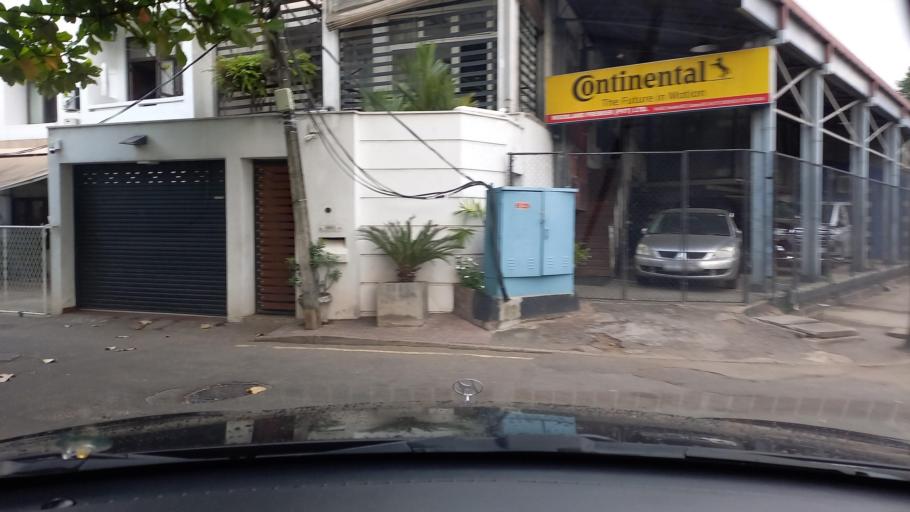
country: LK
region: Western
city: Pita Kotte
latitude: 6.8790
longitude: 79.8693
